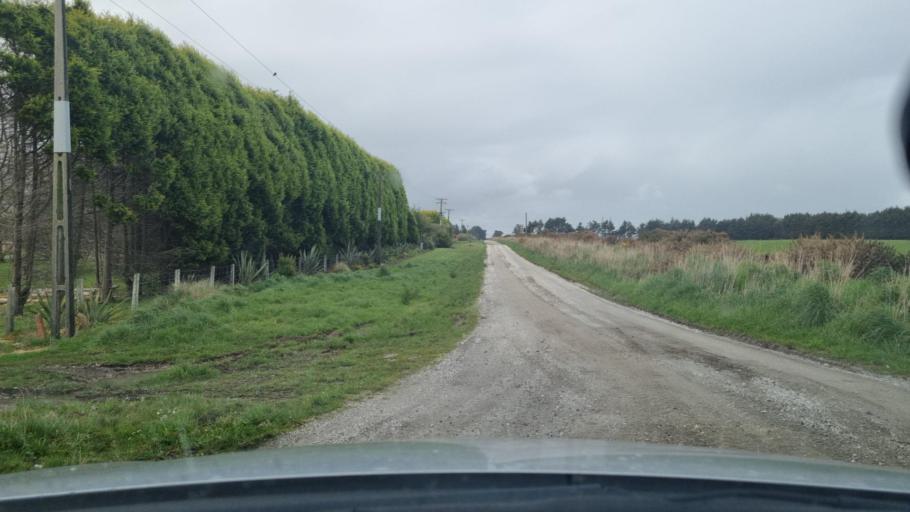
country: NZ
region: Southland
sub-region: Invercargill City
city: Invercargill
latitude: -46.4961
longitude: 168.4191
